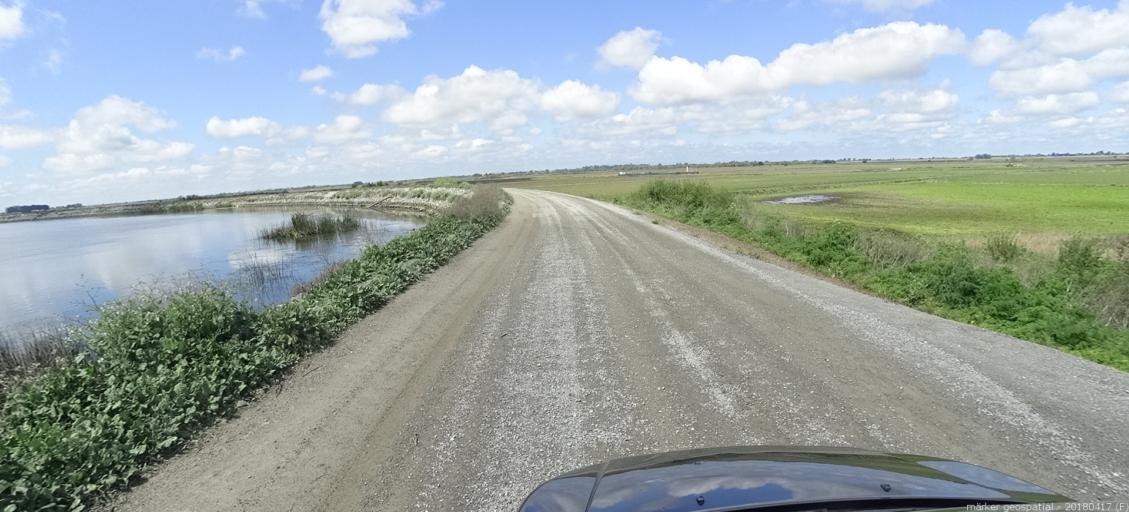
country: US
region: California
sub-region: Sacramento County
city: Walnut Grove
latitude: 38.1524
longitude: -121.5398
